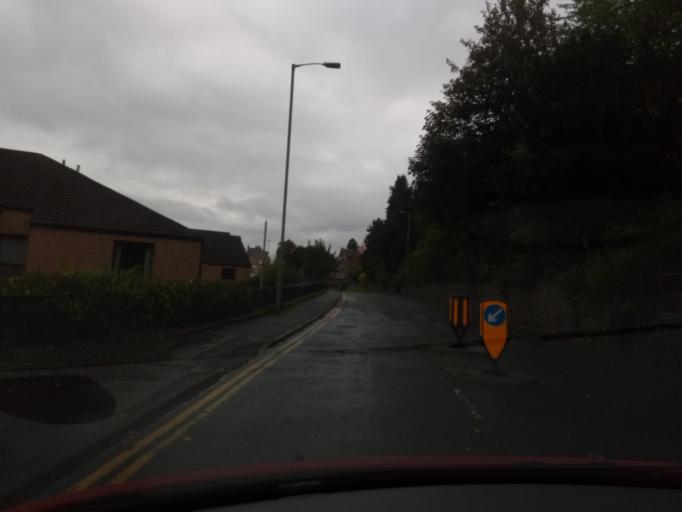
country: GB
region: Scotland
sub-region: The Scottish Borders
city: Galashiels
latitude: 55.6138
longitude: -2.8060
